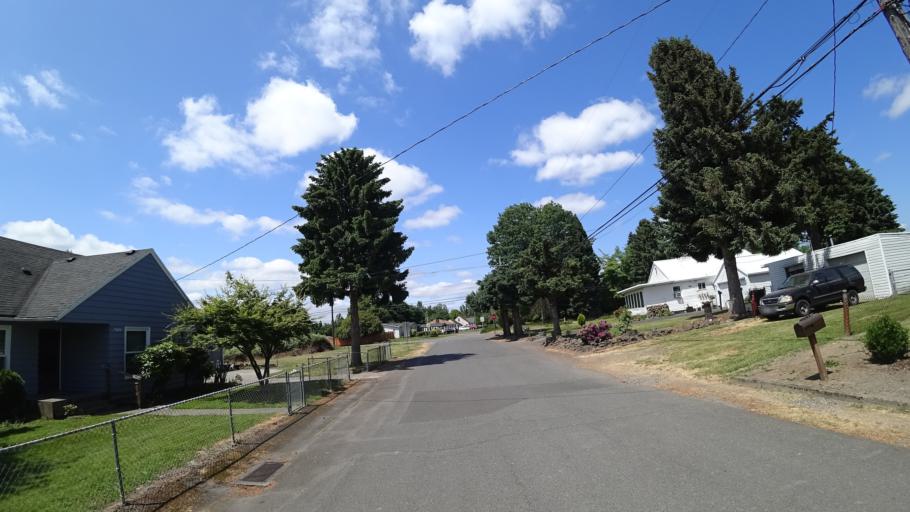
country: US
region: Washington
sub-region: Clark County
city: Vancouver
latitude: 45.5976
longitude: -122.6600
